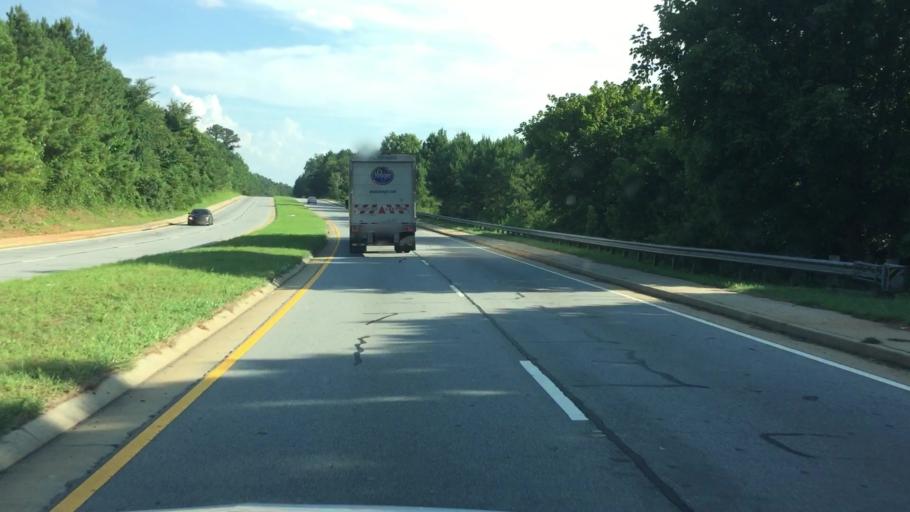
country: US
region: Georgia
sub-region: Gwinnett County
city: Snellville
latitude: 33.7848
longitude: -84.0472
